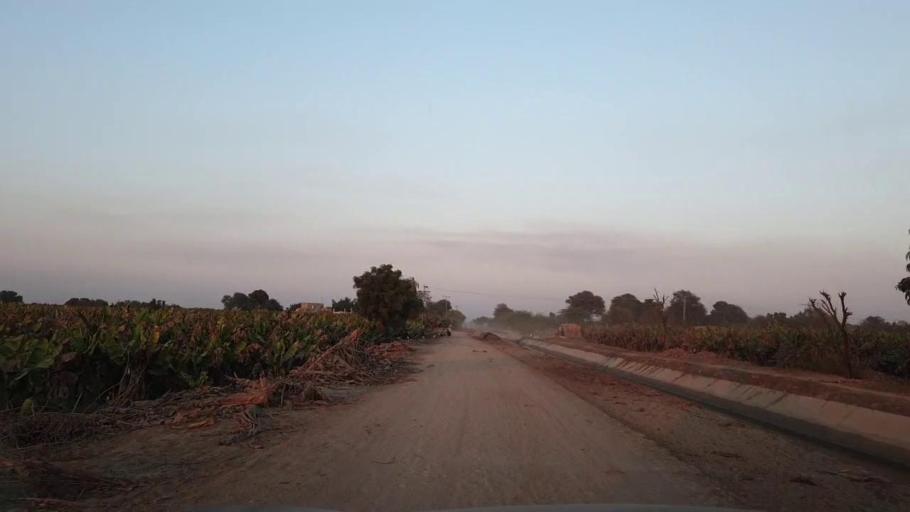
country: PK
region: Sindh
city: Berani
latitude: 25.6641
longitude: 68.7825
